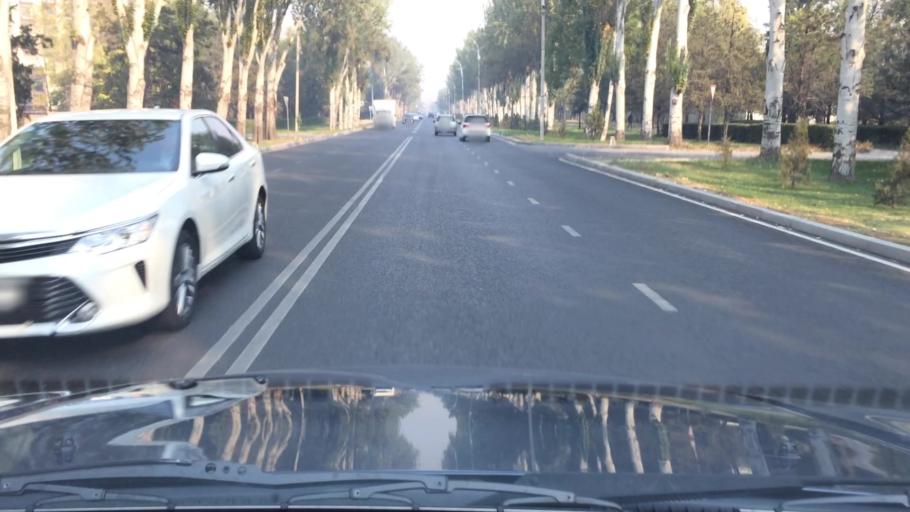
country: KG
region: Chuy
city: Bishkek
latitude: 42.8360
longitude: 74.5856
